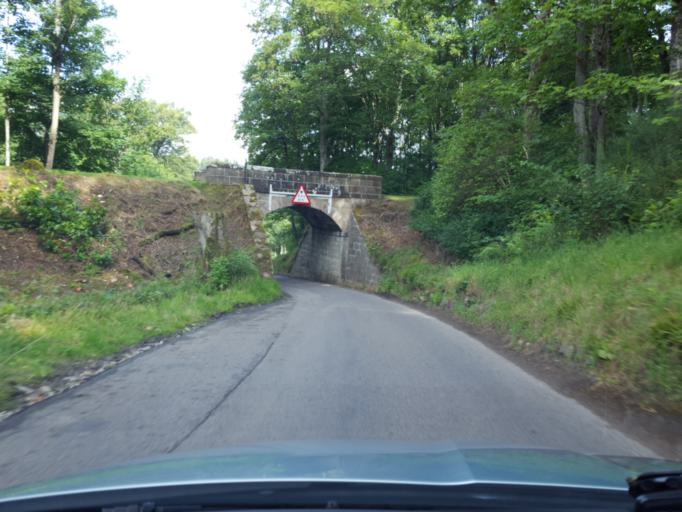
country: GB
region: Scotland
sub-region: Moray
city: Rothes
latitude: 57.4790
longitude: -3.2000
